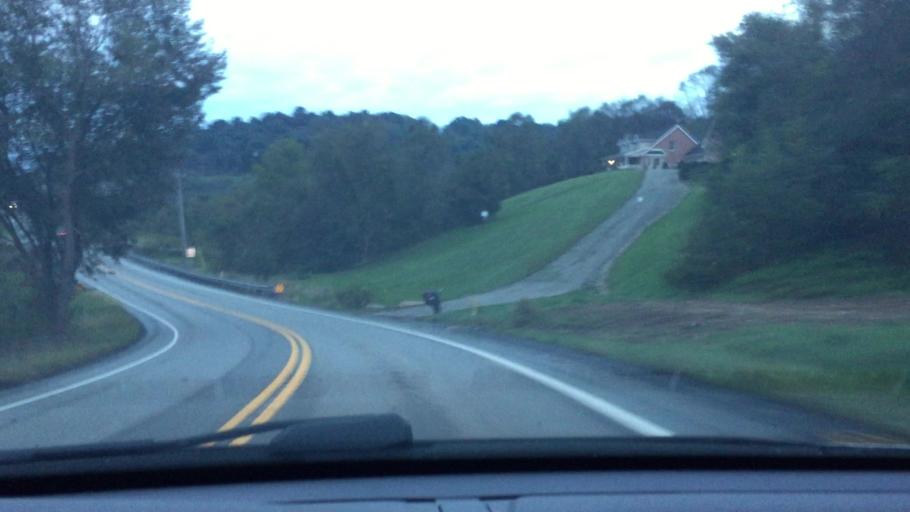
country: US
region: Pennsylvania
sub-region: Washington County
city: McGovern
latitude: 40.1818
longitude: -80.1750
